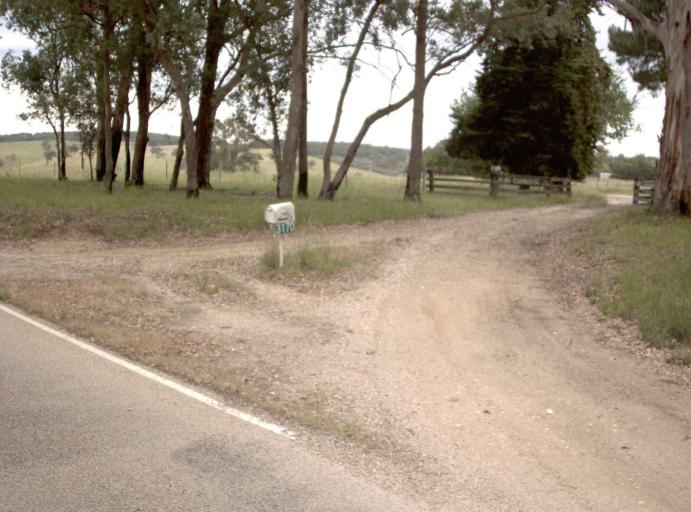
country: AU
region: Victoria
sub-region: East Gippsland
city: Bairnsdale
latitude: -37.7410
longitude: 147.3133
